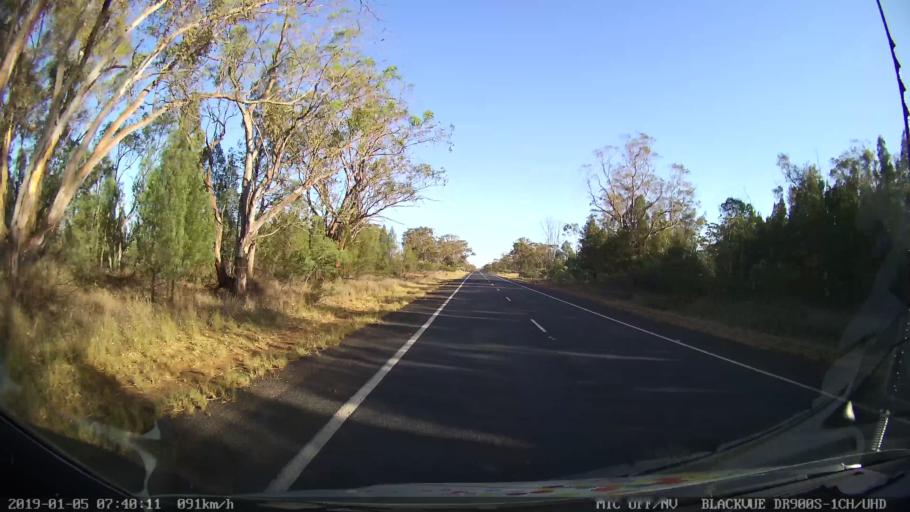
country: AU
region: New South Wales
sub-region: Gilgandra
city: Gilgandra
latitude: -31.9275
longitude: 148.6196
